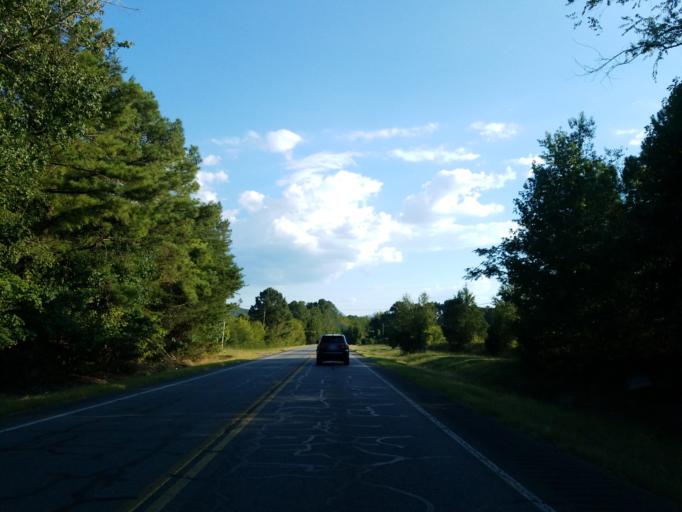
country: US
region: Georgia
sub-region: Murray County
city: Chatsworth
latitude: 34.9219
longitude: -84.7469
